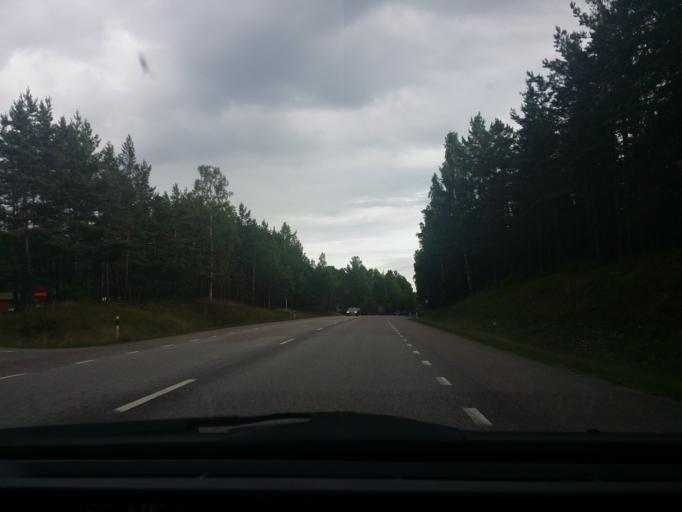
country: SE
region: OErebro
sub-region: Nora Kommun
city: Nora
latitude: 59.4552
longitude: 15.1339
